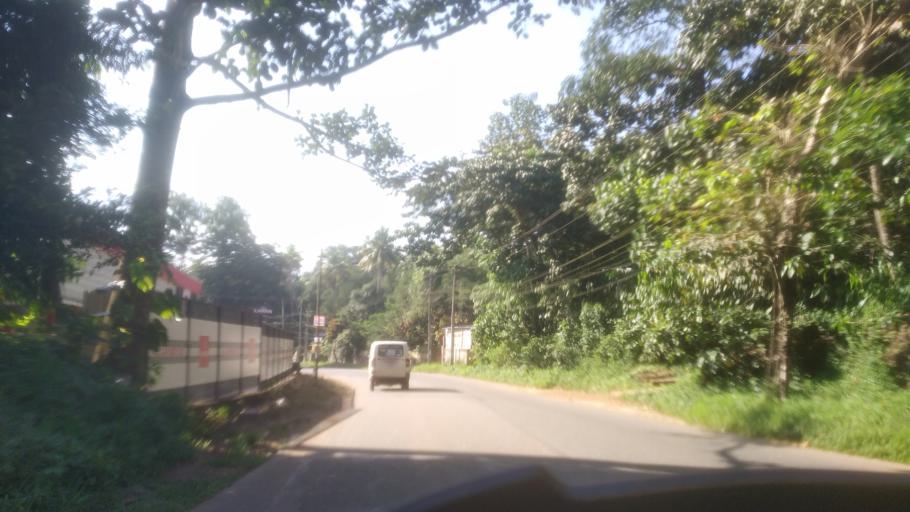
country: IN
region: Kerala
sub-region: Ernakulam
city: Muvattupuzha
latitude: 9.9802
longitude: 76.5475
